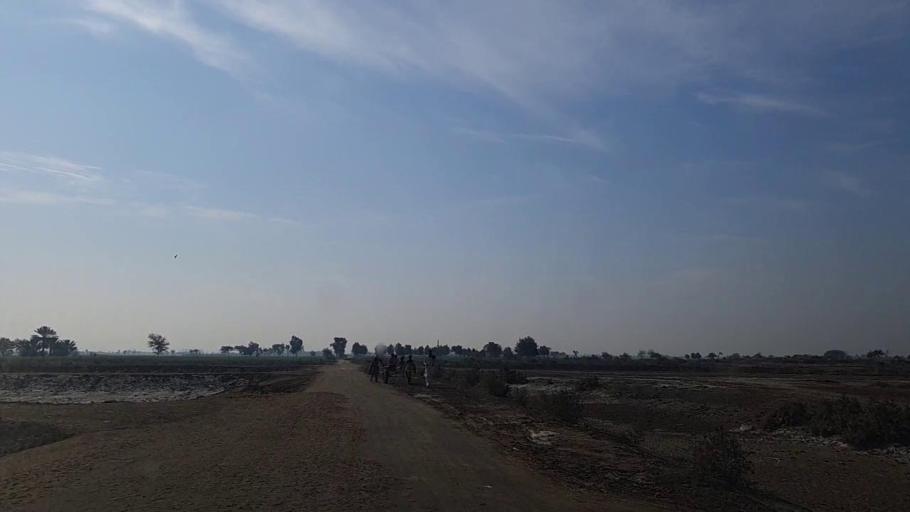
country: PK
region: Sindh
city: Mirpur Khas
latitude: 25.4970
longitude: 69.0000
